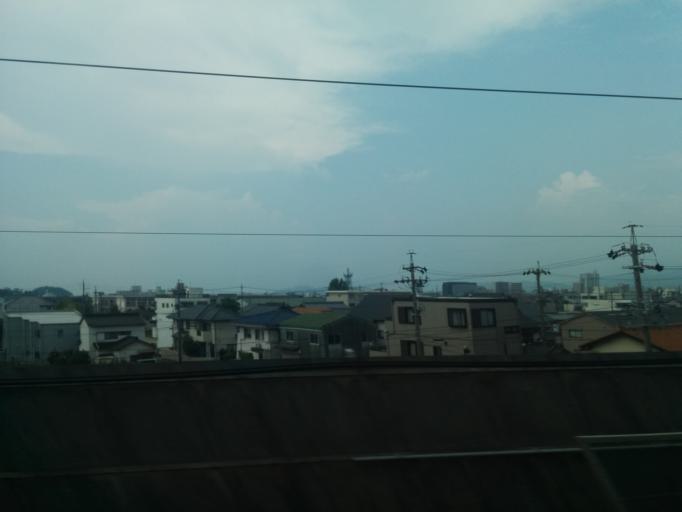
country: JP
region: Aichi
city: Gamagori
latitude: 34.8278
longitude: 137.2385
